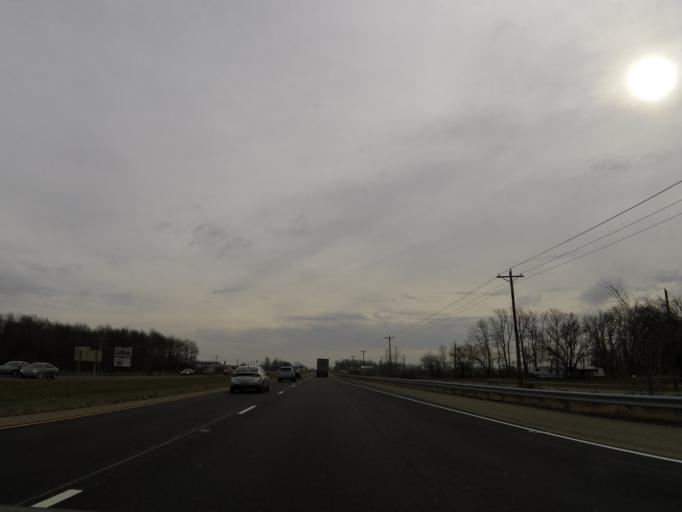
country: US
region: Indiana
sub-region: Shelby County
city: Shelbyville
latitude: 39.5816
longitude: -85.8197
